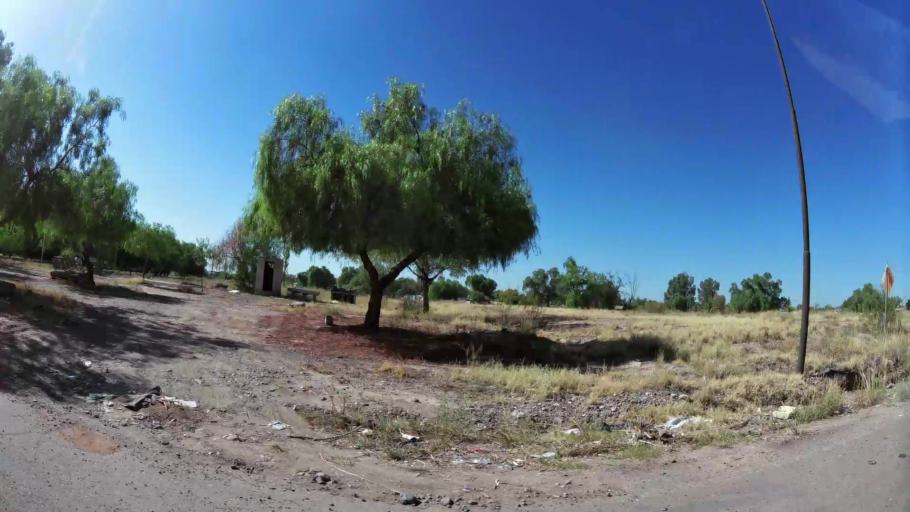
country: AR
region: Mendoza
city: Mendoza
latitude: -32.8990
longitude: -68.8789
